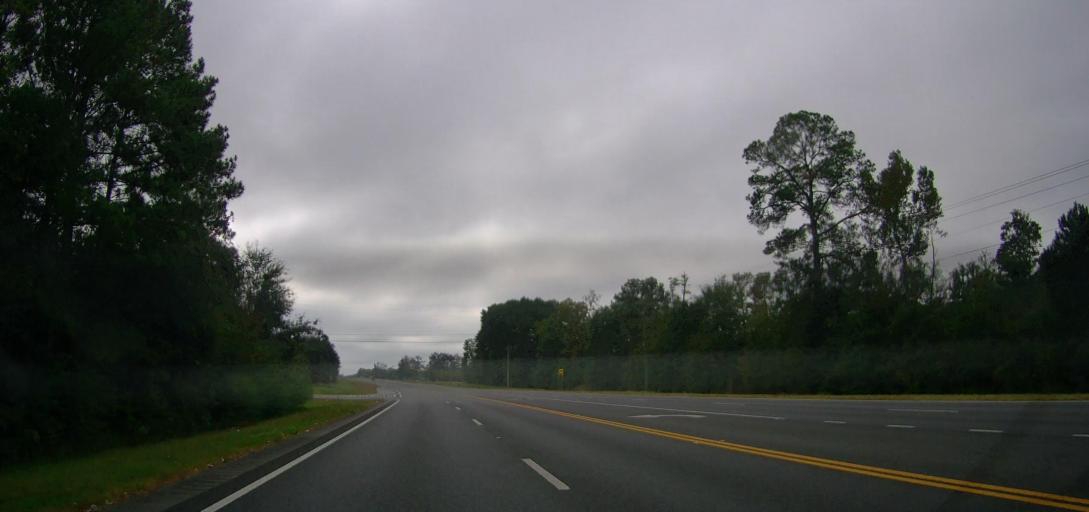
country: US
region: Georgia
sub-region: Thomas County
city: Thomasville
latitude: 30.9694
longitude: -83.8912
